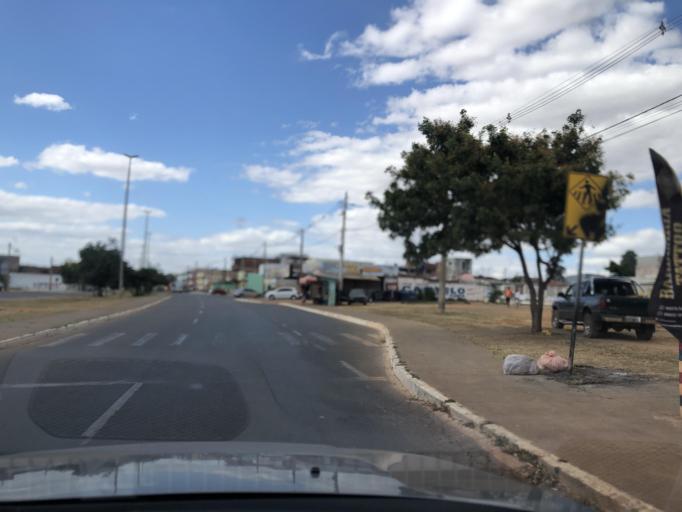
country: BR
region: Federal District
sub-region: Brasilia
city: Brasilia
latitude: -15.8876
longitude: -48.1484
